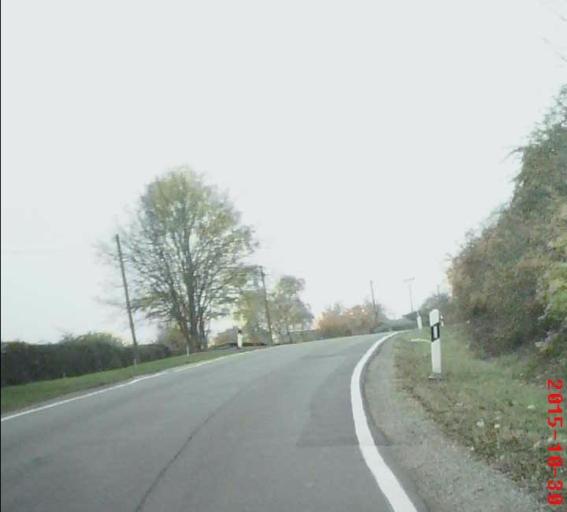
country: DE
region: Thuringia
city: Muehlhausen
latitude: 51.2257
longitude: 10.4295
